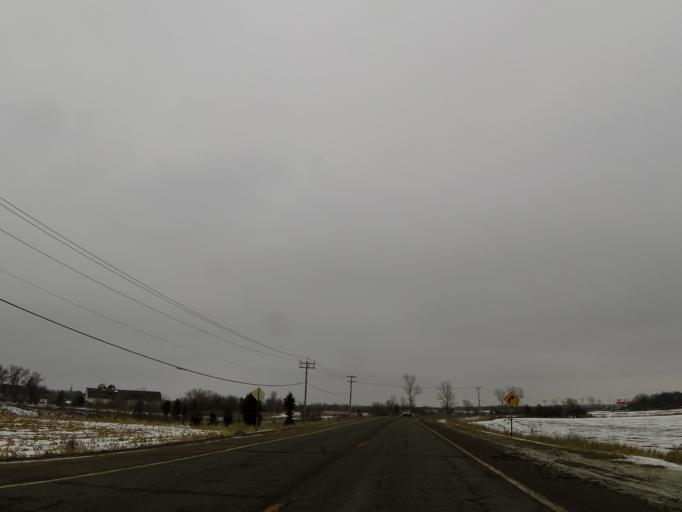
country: US
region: Minnesota
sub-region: Washington County
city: Lakeland
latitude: 44.9542
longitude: -92.7941
